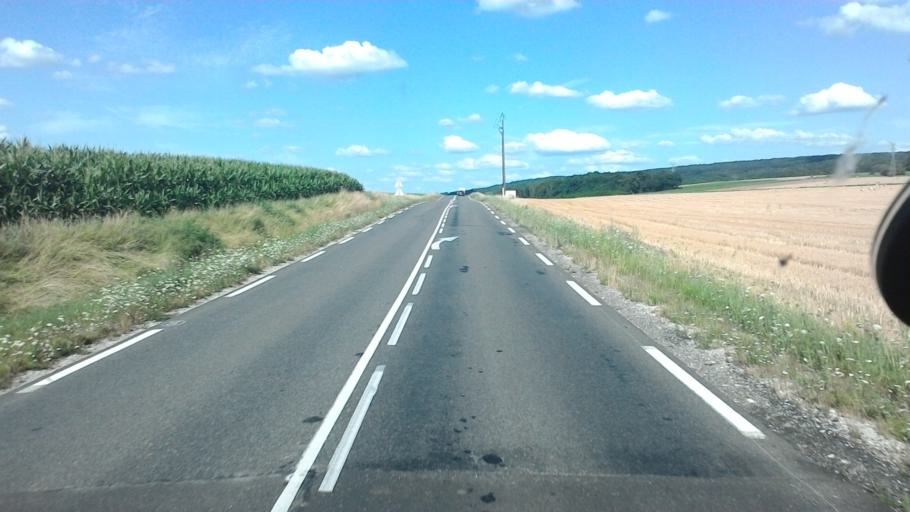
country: FR
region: Franche-Comte
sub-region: Departement de la Haute-Saone
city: Gy
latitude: 47.3832
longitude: 5.7779
